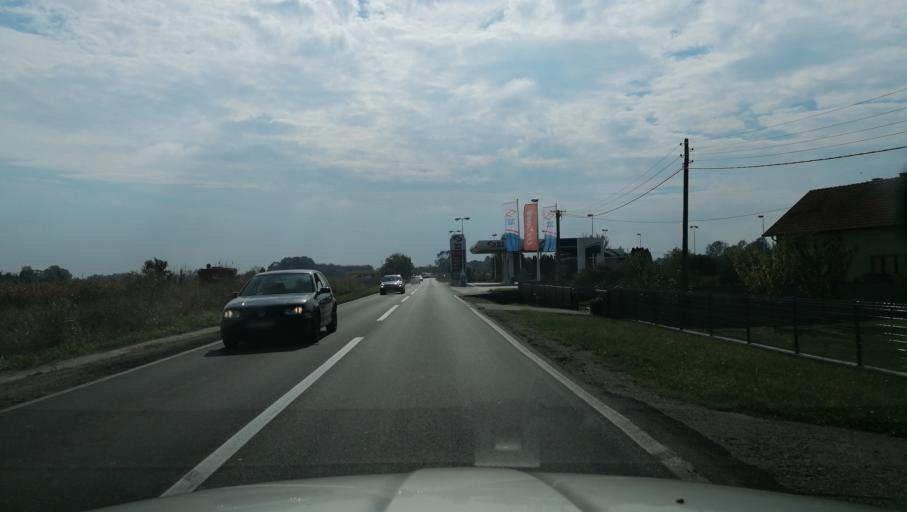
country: BA
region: Republika Srpska
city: Dvorovi
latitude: 44.8375
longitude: 19.2963
